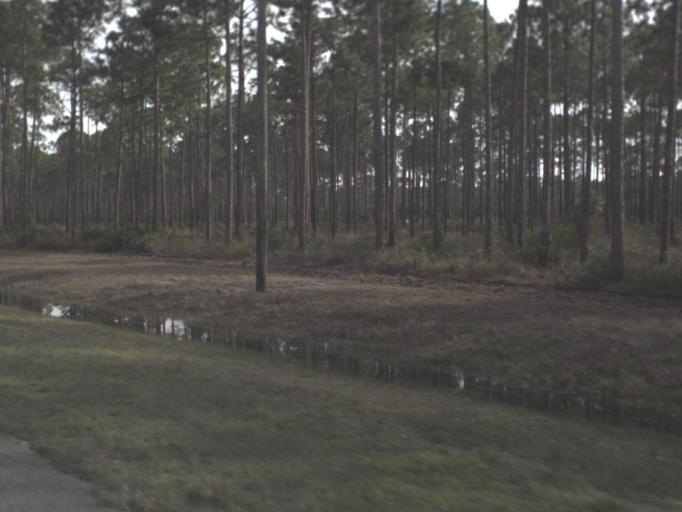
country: US
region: Florida
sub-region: Bay County
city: Mexico Beach
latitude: 29.9871
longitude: -85.4828
